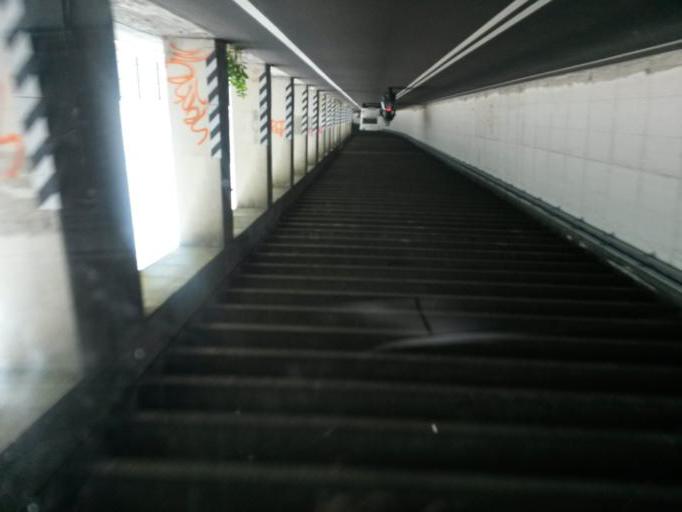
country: IT
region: Trentino-Alto Adige
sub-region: Provincia di Trento
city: Torbole sul Garda
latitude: 45.8213
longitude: 10.8575
